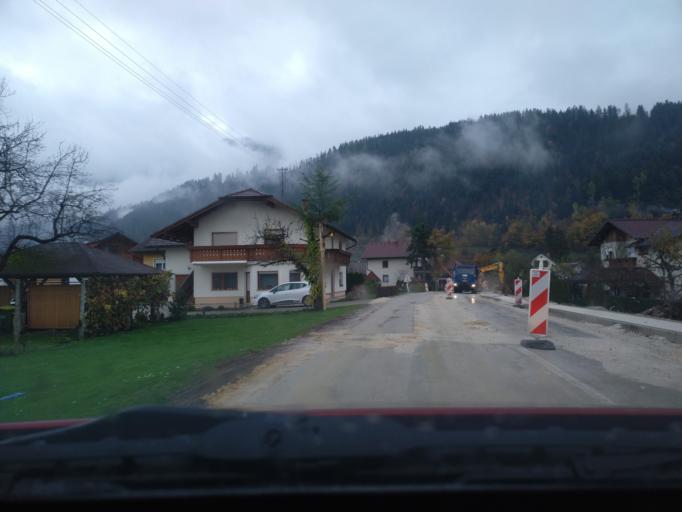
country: SI
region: Ljubno
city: Ljubno ob Savinji
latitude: 46.3336
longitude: 14.8538
